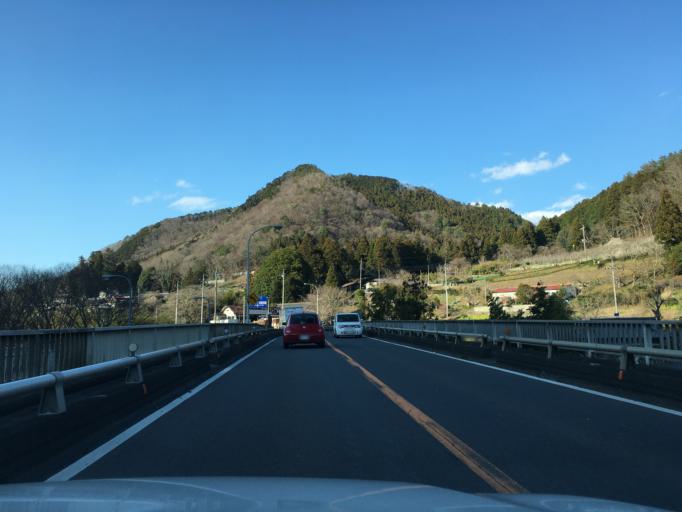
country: JP
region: Ibaraki
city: Daigo
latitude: 36.6924
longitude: 140.3892
